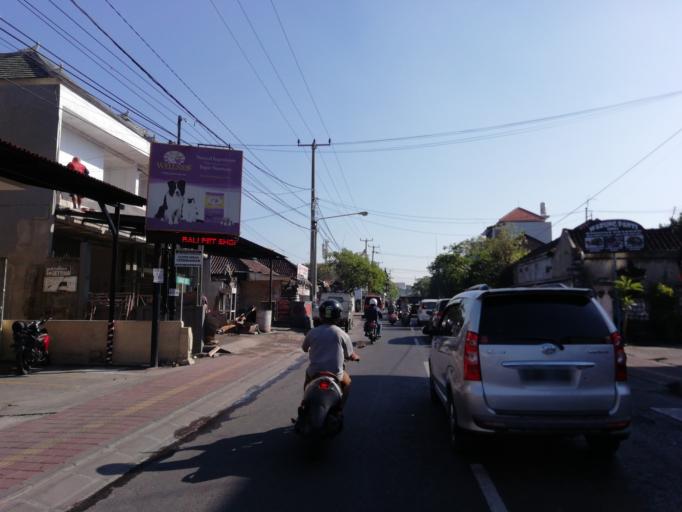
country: ID
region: Bali
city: Denpasar
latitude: -8.6527
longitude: 115.2086
